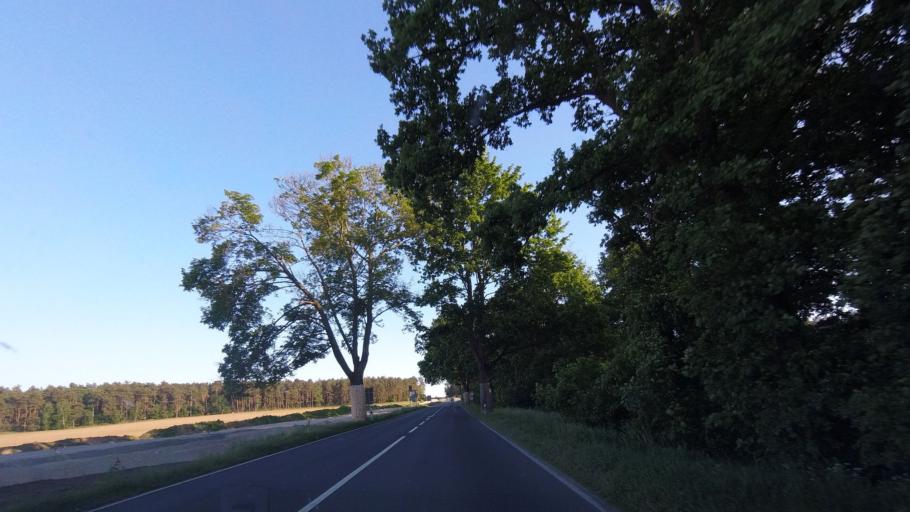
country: DE
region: Brandenburg
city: Brandenburg an der Havel
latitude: 52.3609
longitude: 12.5973
